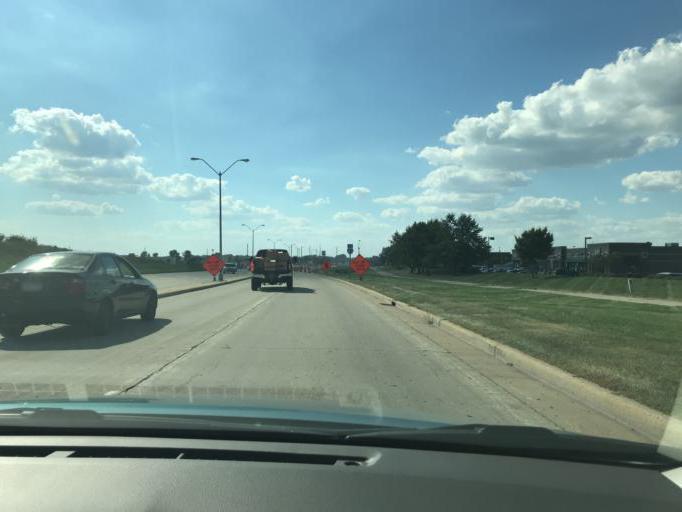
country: US
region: Wisconsin
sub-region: Walworth County
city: Delavan
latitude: 42.6280
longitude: -88.6104
